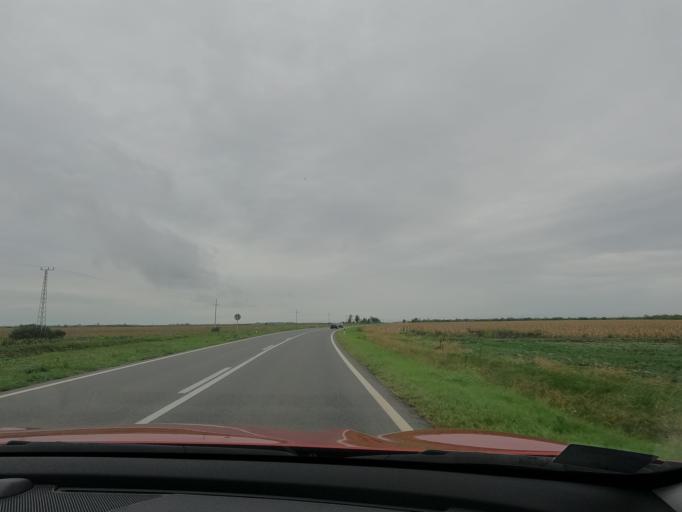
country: RS
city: Banatska Topola
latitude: 45.7116
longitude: 20.4175
